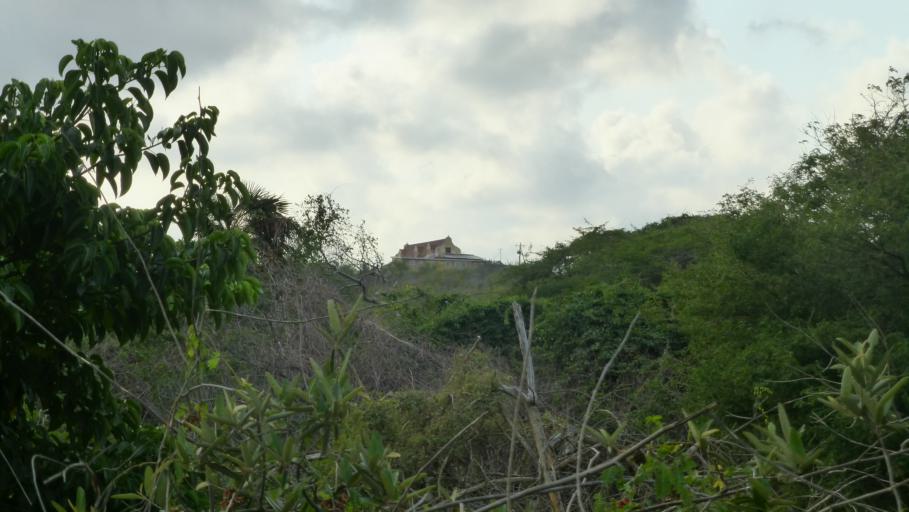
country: CW
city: Sint Michiel Liber
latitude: 12.1659
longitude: -68.9988
